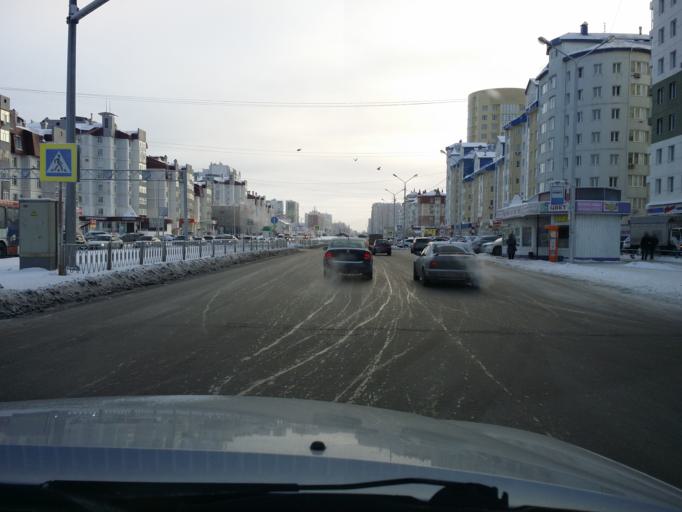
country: RU
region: Khanty-Mansiyskiy Avtonomnyy Okrug
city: Nizhnevartovsk
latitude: 60.9381
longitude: 76.5762
